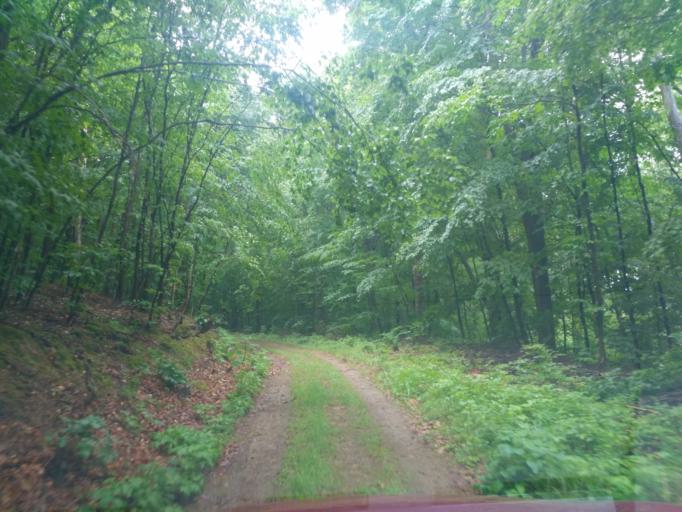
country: SK
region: Kosicky
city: Moldava nad Bodvou
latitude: 48.6975
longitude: 21.0722
